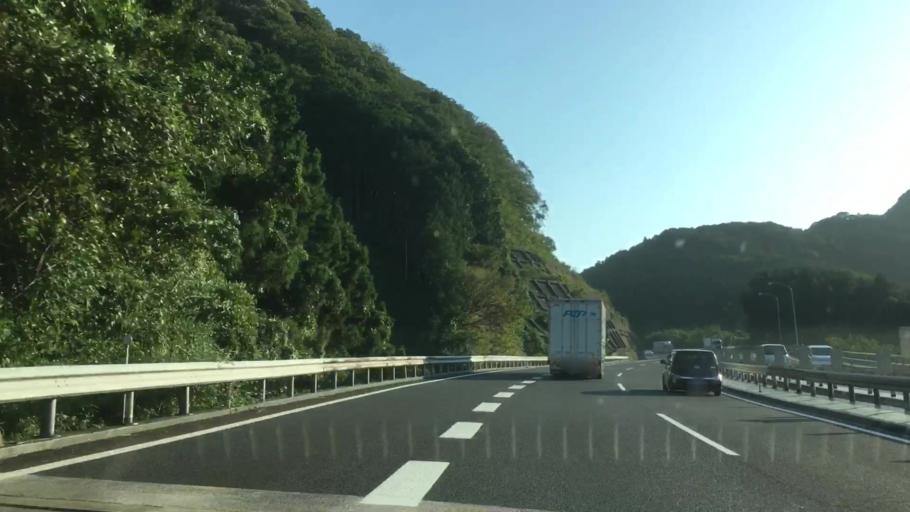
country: JP
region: Yamaguchi
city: Onoda
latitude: 34.1528
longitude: 131.2355
